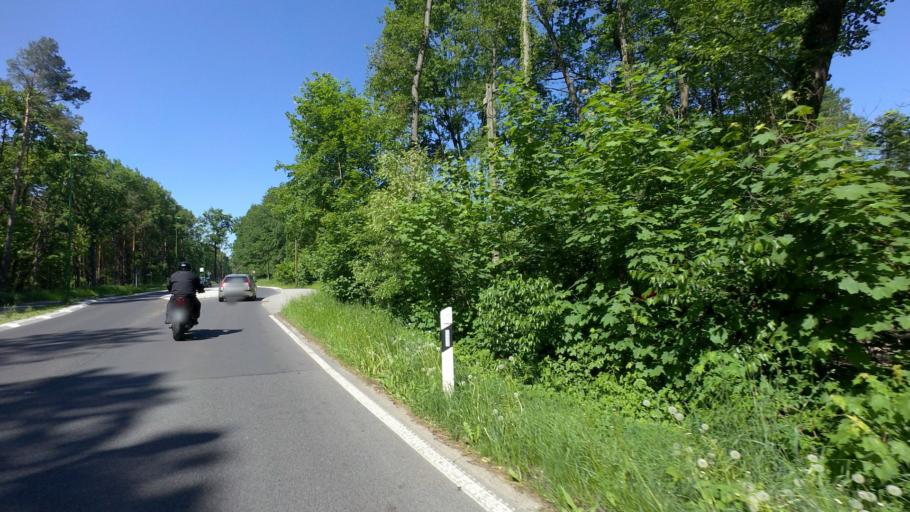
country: DE
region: Brandenburg
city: Bestensee
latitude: 52.2582
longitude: 13.6374
